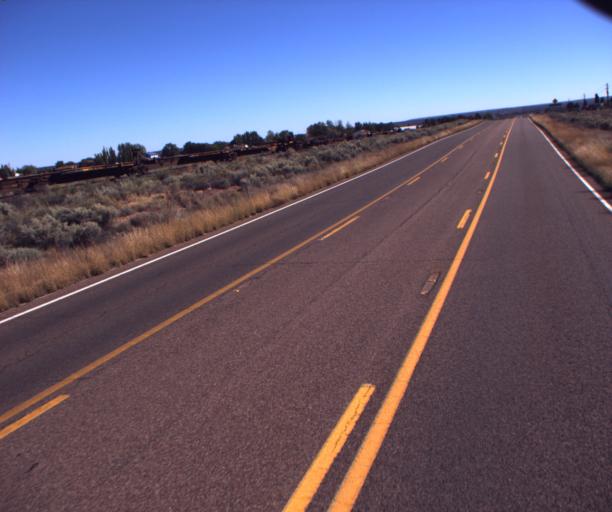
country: US
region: Arizona
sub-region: Navajo County
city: Snowflake
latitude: 34.5130
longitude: -110.1256
